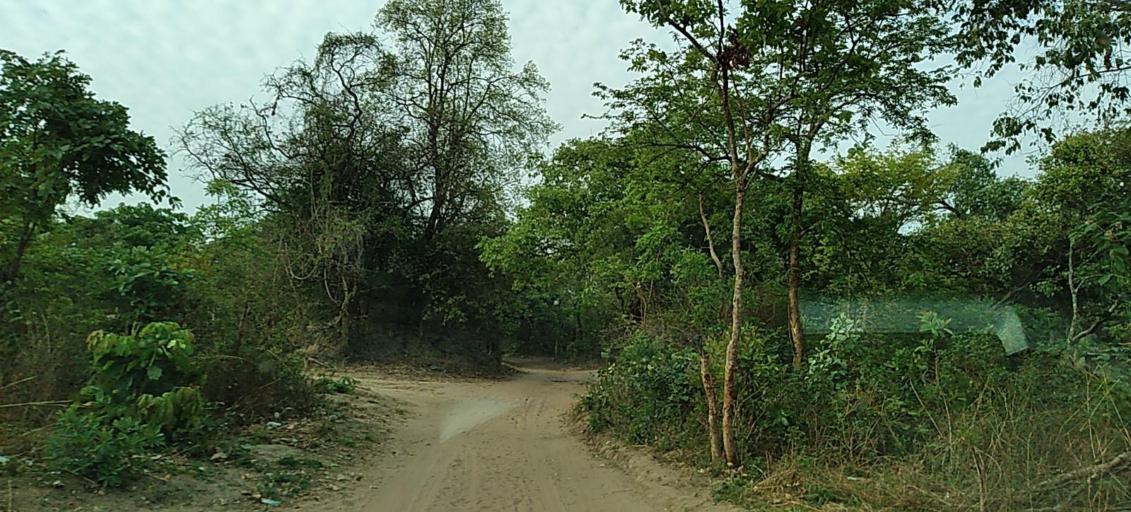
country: ZM
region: Copperbelt
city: Kalulushi
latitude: -12.9127
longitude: 27.6886
